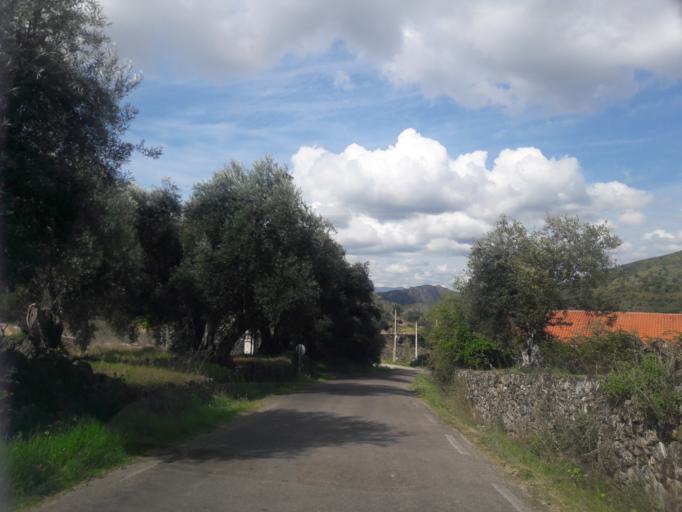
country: ES
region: Castille and Leon
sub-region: Provincia de Salamanca
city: San Esteban de la Sierra
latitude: 40.5062
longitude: -5.9002
